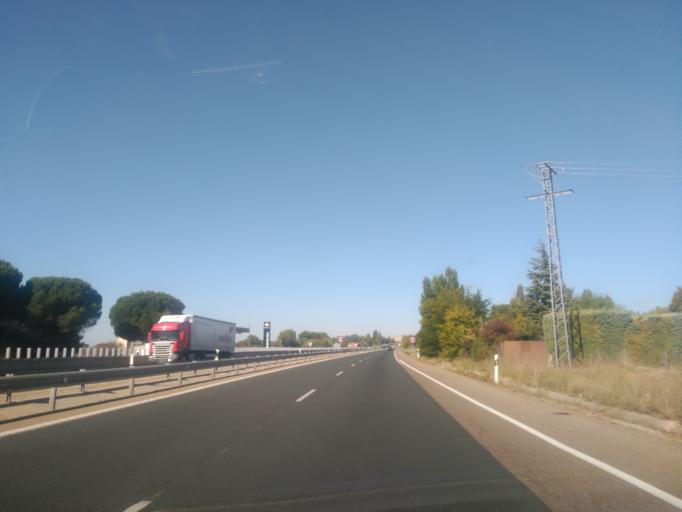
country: ES
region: Castille and Leon
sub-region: Provincia de Valladolid
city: Tudela de Duero
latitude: 41.5914
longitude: -4.6056
